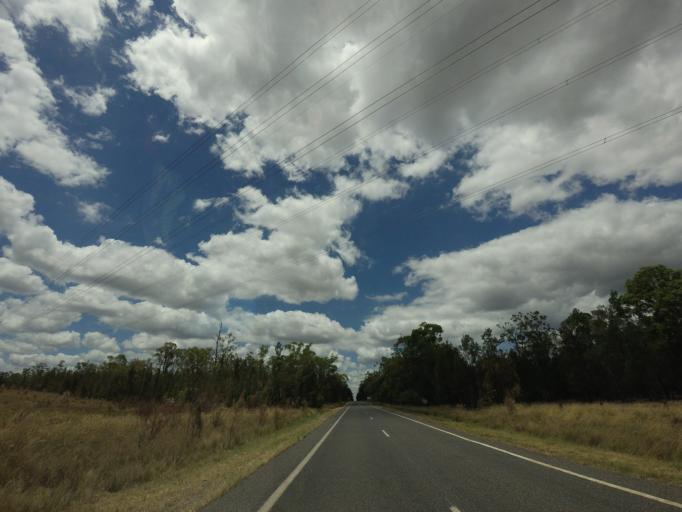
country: AU
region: Queensland
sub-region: Goondiwindi
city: Goondiwindi
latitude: -28.0235
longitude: 150.8475
